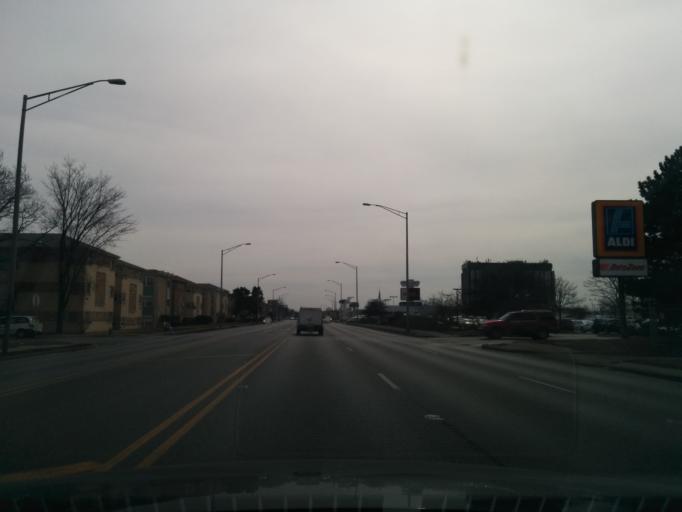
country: US
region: Illinois
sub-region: Cook County
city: Berwyn
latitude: 41.8543
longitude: -87.8038
